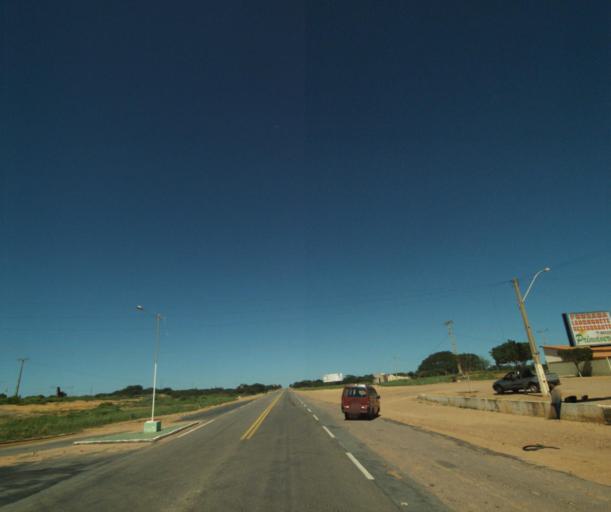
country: BR
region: Bahia
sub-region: Palmas De Monte Alto
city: Palmas de Monte Alto
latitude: -14.2500
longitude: -43.1685
